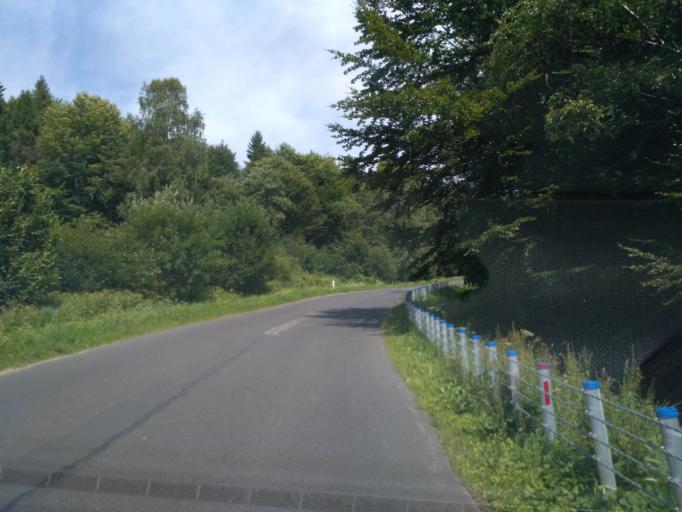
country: PL
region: Subcarpathian Voivodeship
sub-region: Powiat bieszczadzki
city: Czarna
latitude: 49.3106
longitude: 22.6087
